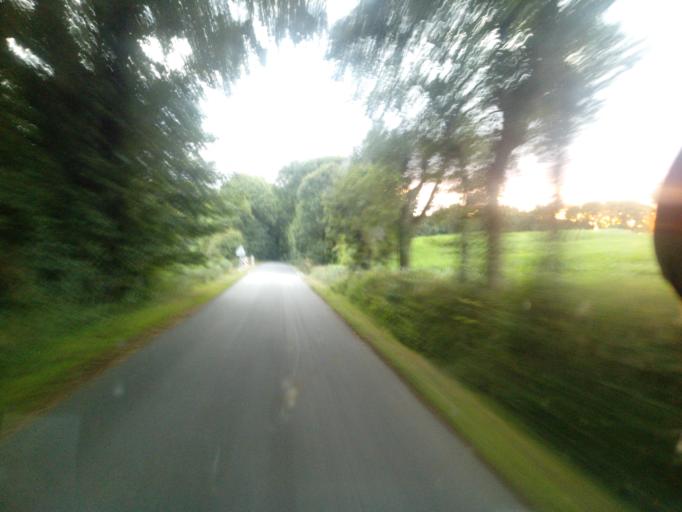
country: FR
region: Brittany
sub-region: Departement du Morbihan
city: Guegon
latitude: 47.9126
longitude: -2.6011
